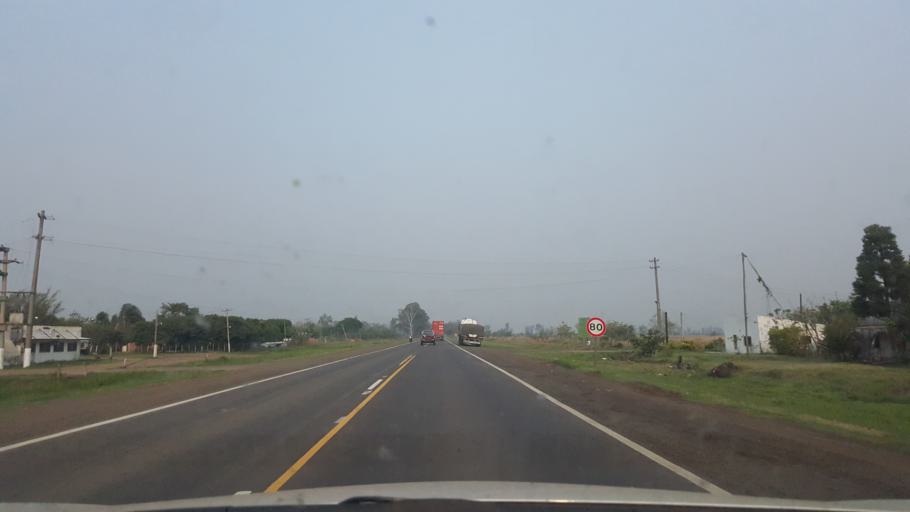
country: AR
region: Corrientes
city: Ita Ibate
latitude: -27.4453
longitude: -57.3364
